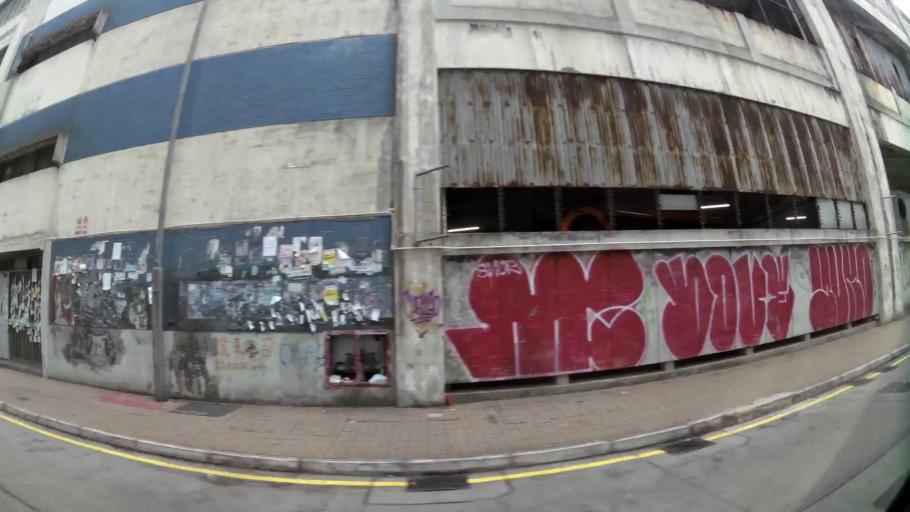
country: HK
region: Kowloon City
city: Kowloon
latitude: 22.3131
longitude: 114.2216
